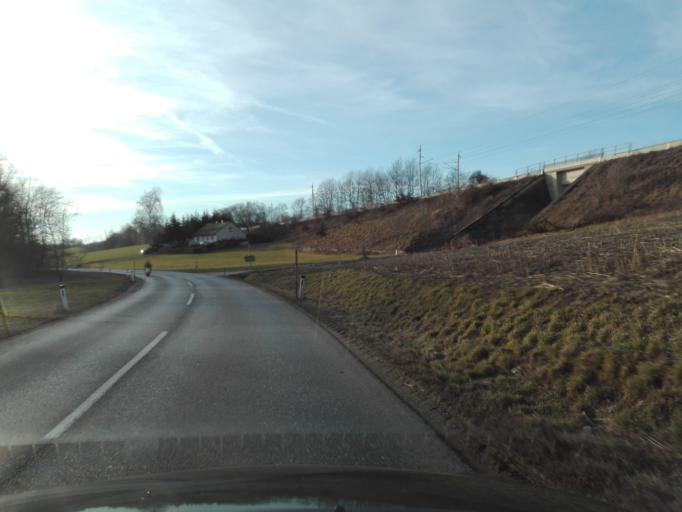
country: AT
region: Lower Austria
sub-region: Politischer Bezirk Amstetten
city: Haag
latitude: 48.1166
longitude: 14.5473
